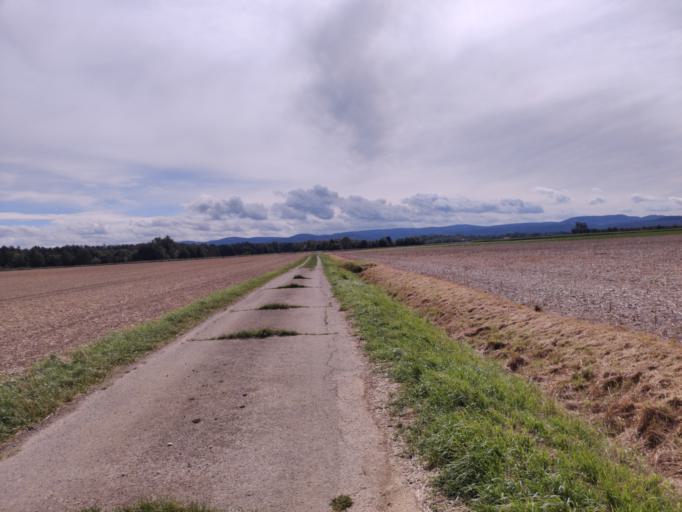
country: DE
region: Lower Saxony
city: Langelsheim
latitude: 51.9843
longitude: 10.3663
